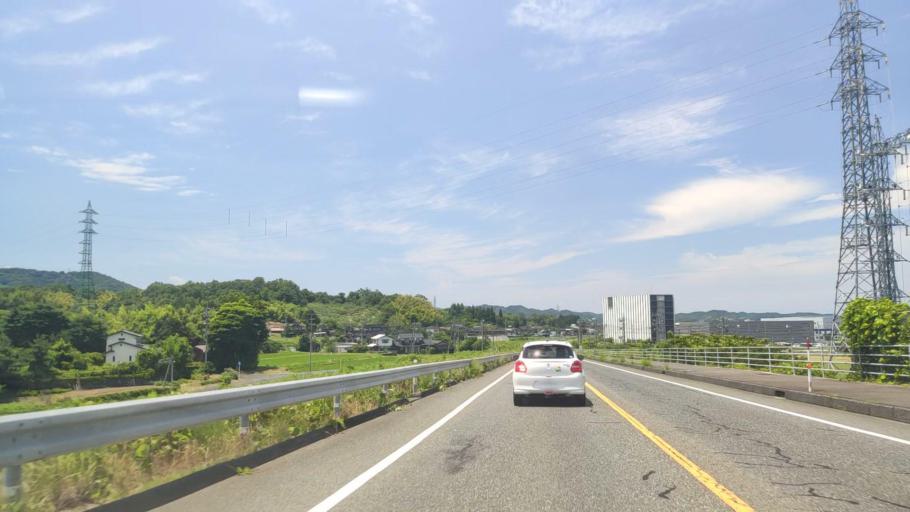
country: JP
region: Tottori
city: Tottori
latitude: 35.4495
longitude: 134.2519
